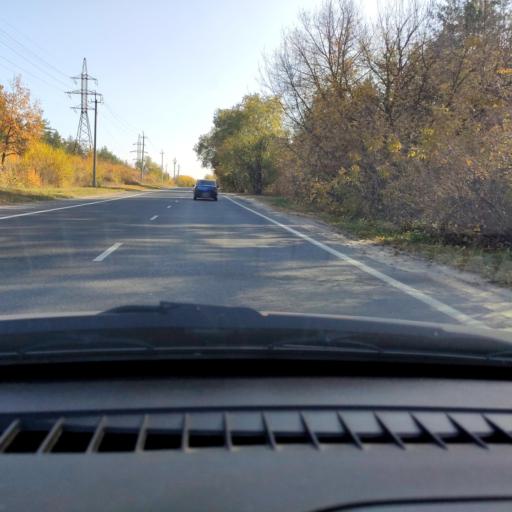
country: RU
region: Samara
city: Zhigulevsk
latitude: 53.5057
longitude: 49.4602
